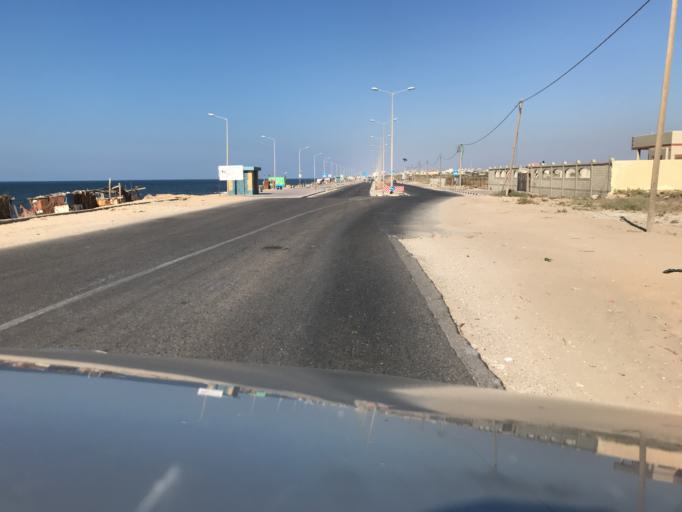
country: PS
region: Gaza Strip
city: An Nusayrat
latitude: 31.4698
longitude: 34.3820
